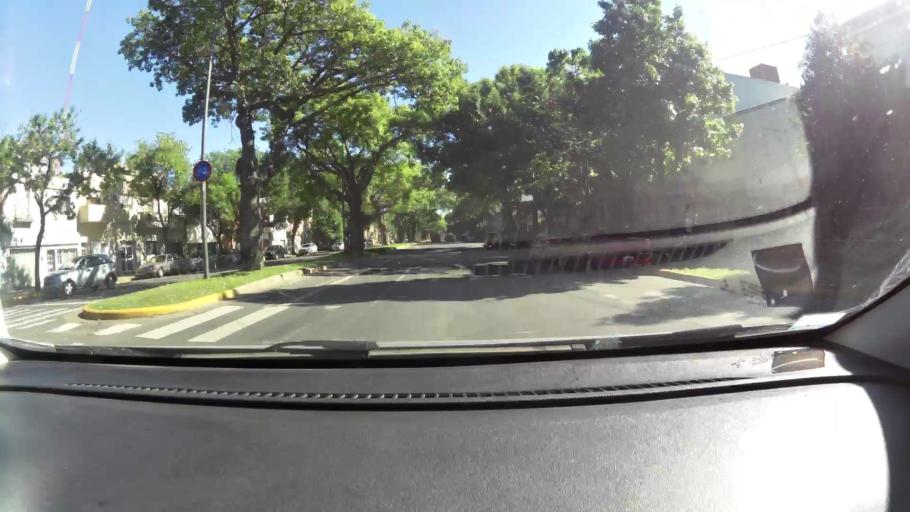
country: AR
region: Santa Fe
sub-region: Departamento de Rosario
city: Rosario
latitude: -32.9604
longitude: -60.6702
